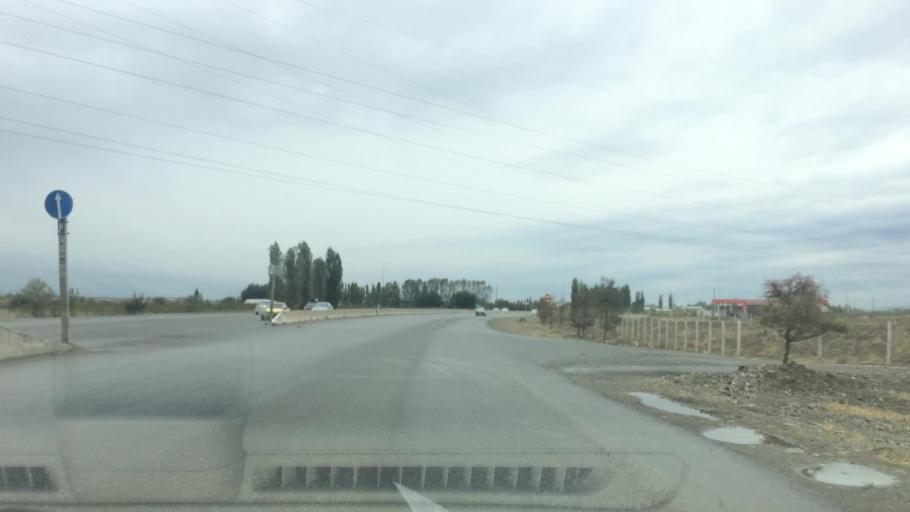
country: UZ
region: Jizzax
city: Jizzax
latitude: 40.0245
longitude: 67.6156
